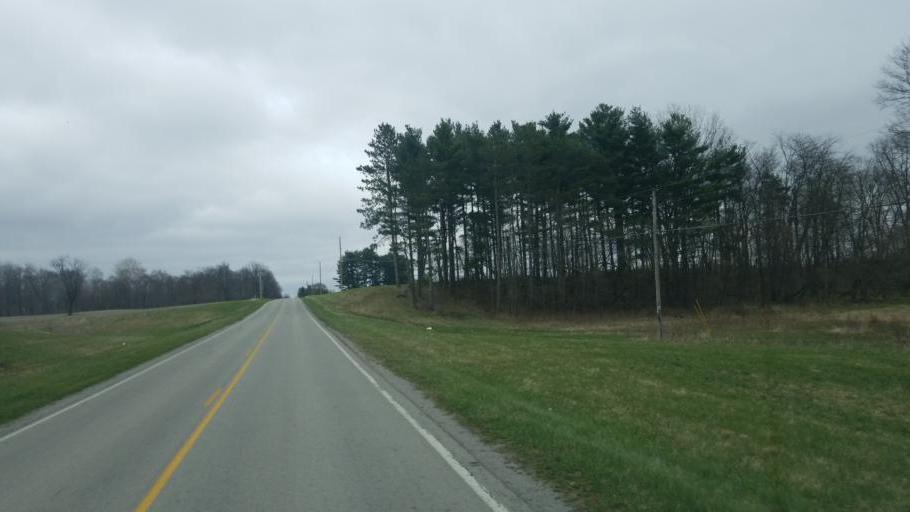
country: US
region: Ohio
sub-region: Wyandot County
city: Upper Sandusky
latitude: 40.8262
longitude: -83.1509
